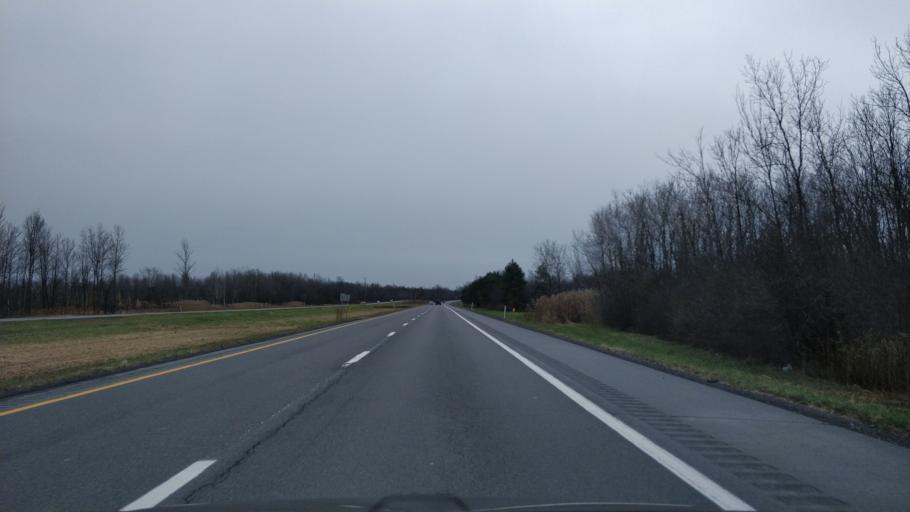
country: US
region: New York
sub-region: Jefferson County
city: Adams Center
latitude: 43.8567
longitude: -76.0183
